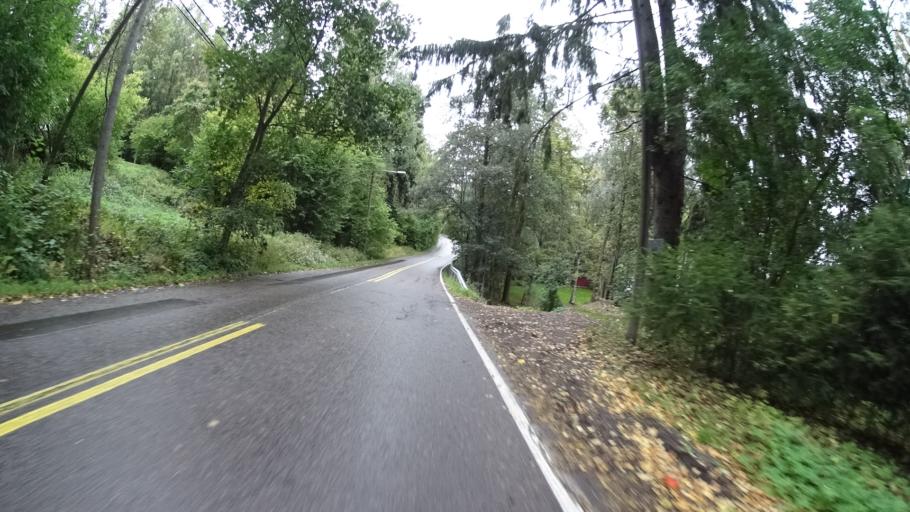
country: FI
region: Uusimaa
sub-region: Helsinki
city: Espoo
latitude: 60.2632
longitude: 24.6547
